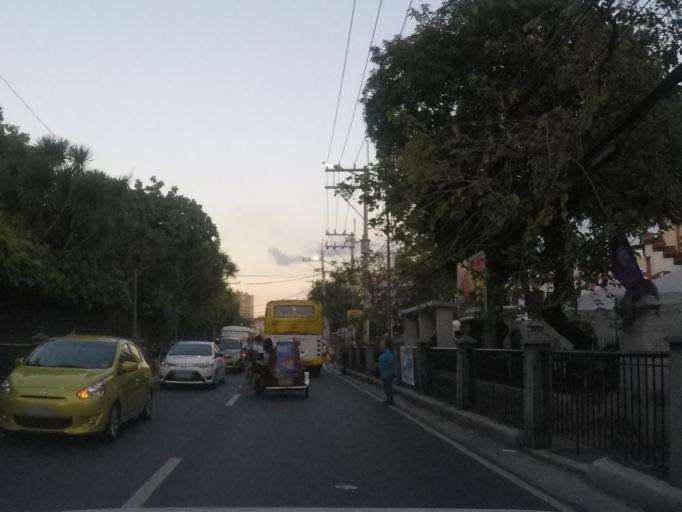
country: PH
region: Metro Manila
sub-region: San Juan
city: San Juan
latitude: 14.6052
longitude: 121.0283
